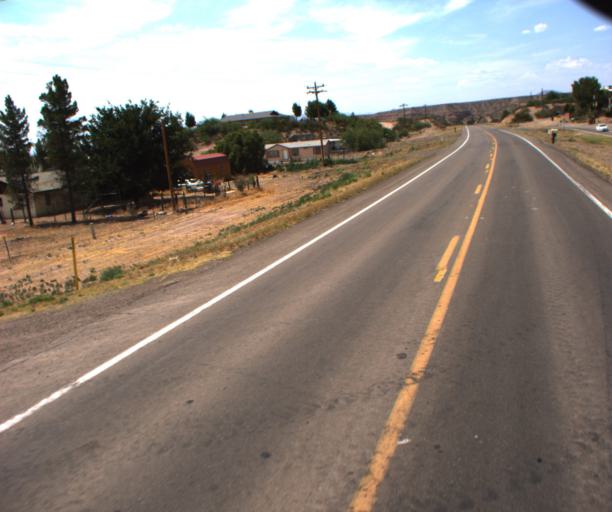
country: US
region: Arizona
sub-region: Greenlee County
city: Clifton
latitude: 32.9171
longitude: -109.1977
